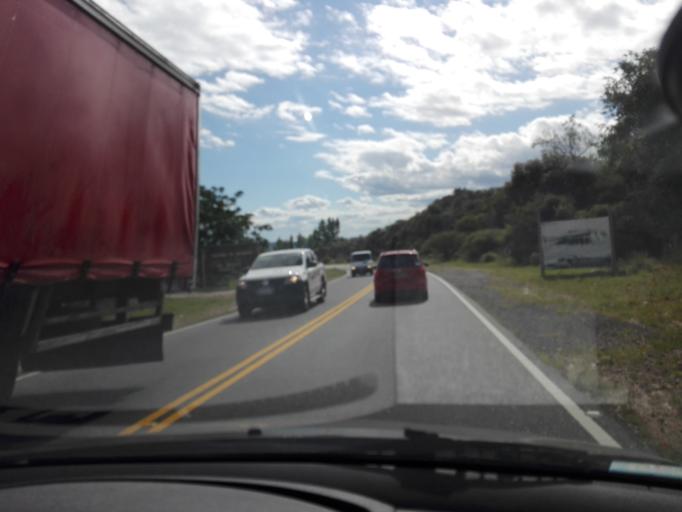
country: AR
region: Cordoba
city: Mina Clavero
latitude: -31.7601
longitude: -64.9609
